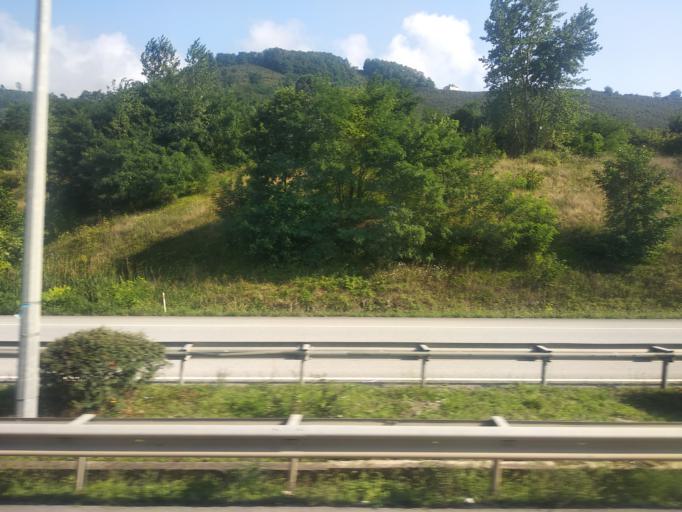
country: TR
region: Ordu
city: Ordu
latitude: 41.0137
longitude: 37.8371
